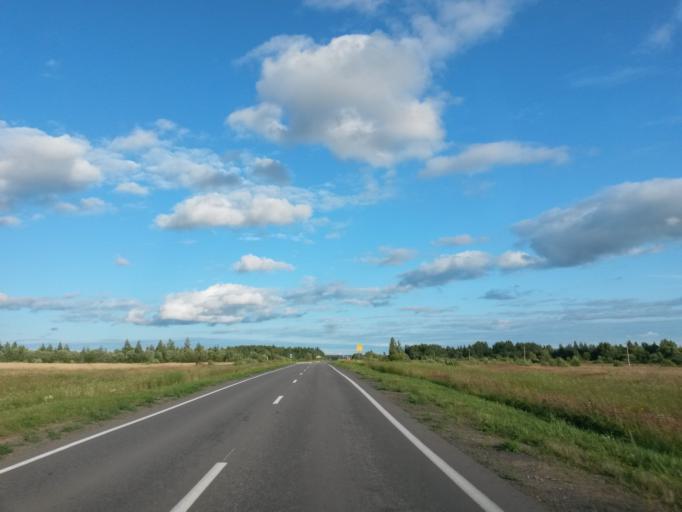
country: RU
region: Jaroslavl
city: Konstantinovskiy
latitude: 57.8719
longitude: 39.5937
